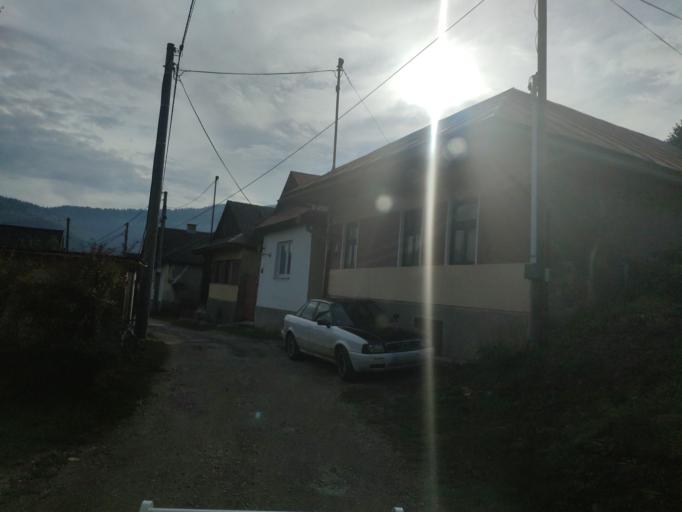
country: SK
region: Presovsky
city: Spisske Podhradie
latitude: 48.8179
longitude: 20.7129
